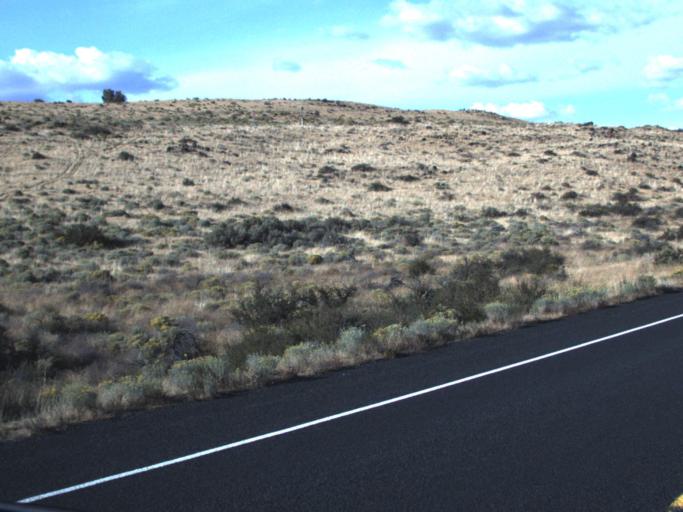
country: US
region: Oregon
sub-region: Morrow County
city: Boardman
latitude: 45.8529
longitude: -119.8635
